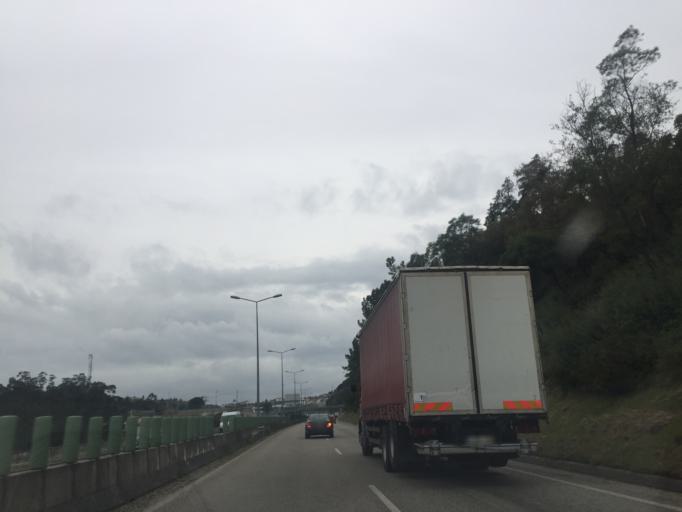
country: PT
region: Coimbra
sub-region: Coimbra
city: Coimbra
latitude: 40.1832
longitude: -8.4388
